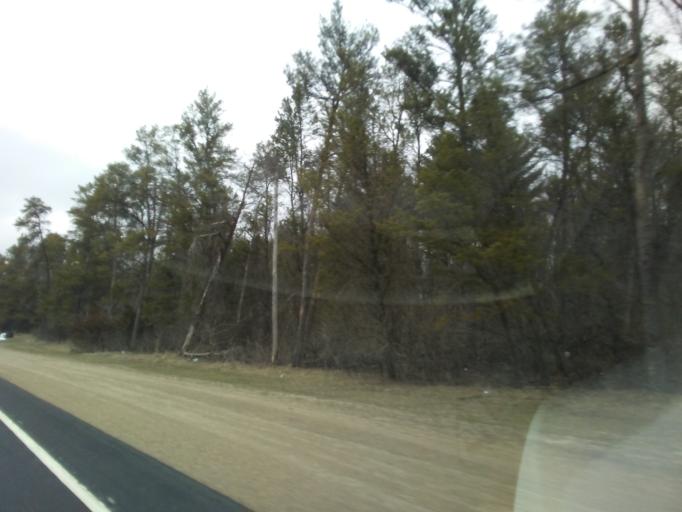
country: US
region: Wisconsin
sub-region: Richland County
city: Richland Center
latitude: 43.2125
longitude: -90.2746
